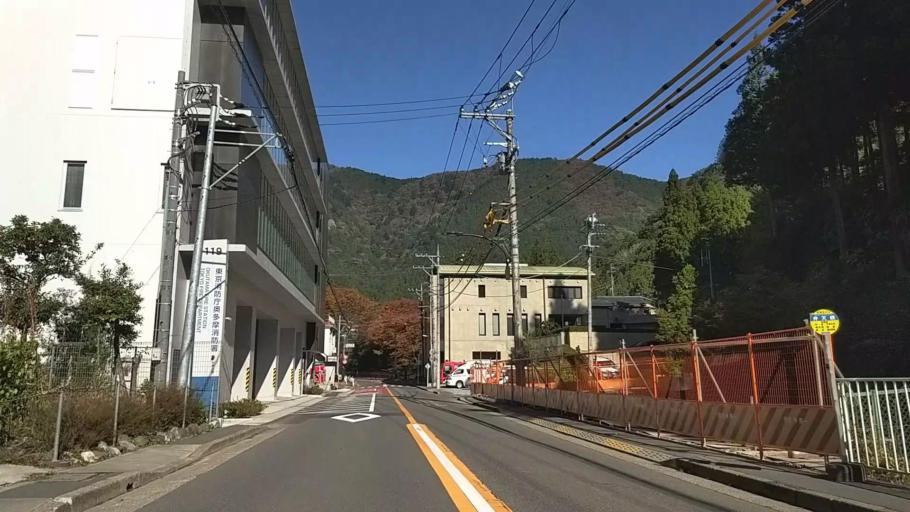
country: JP
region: Tokyo
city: Itsukaichi
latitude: 35.8039
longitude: 139.0923
